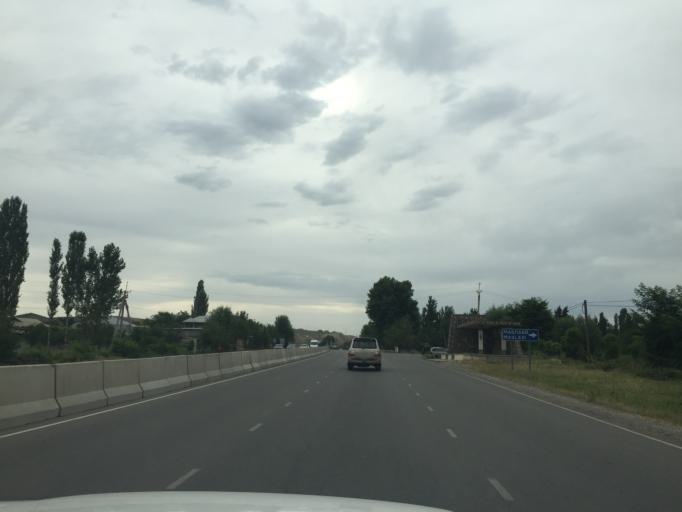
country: TJ
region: Republican Subordination
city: Vahdat
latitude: 38.5560
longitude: 68.9454
